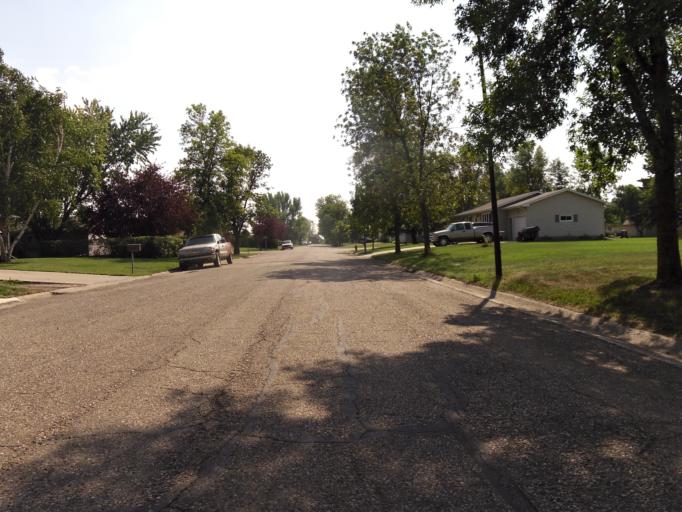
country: US
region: North Dakota
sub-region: Walsh County
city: Grafton
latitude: 48.4171
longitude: -97.3981
